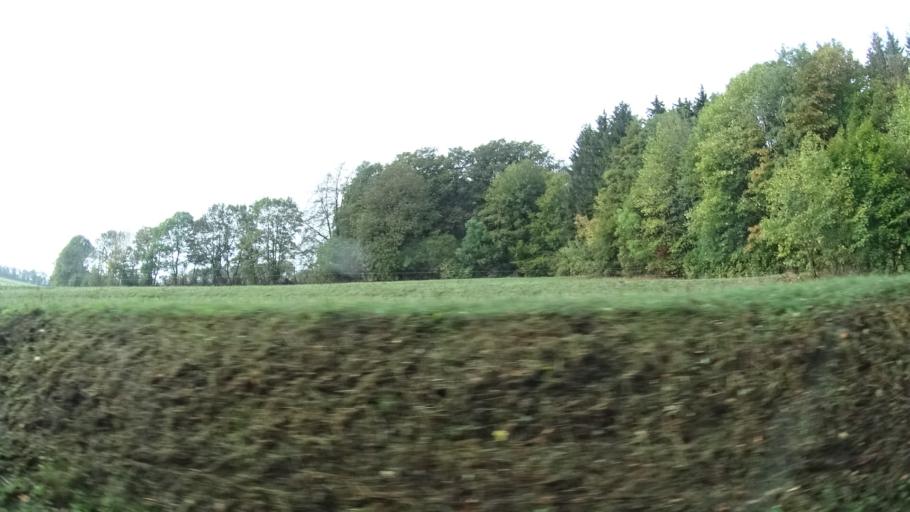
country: DE
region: Hesse
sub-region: Regierungsbezirk Kassel
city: Hofbieber
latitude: 50.5699
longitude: 9.9035
